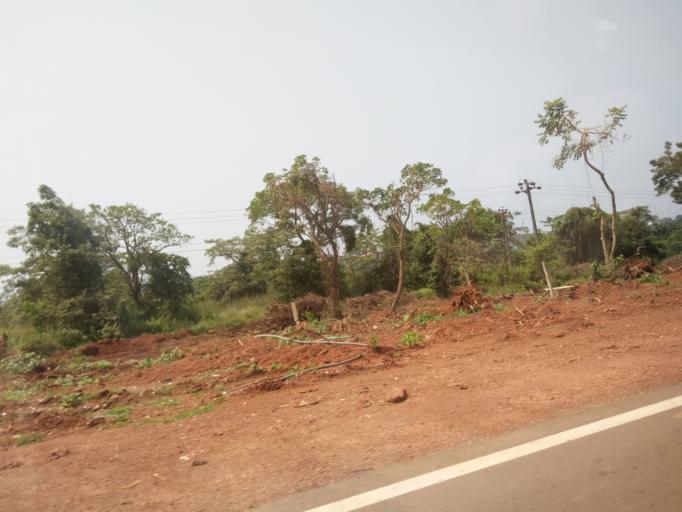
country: IN
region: Goa
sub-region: North Goa
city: Bambolim
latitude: 15.4564
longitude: 73.8660
